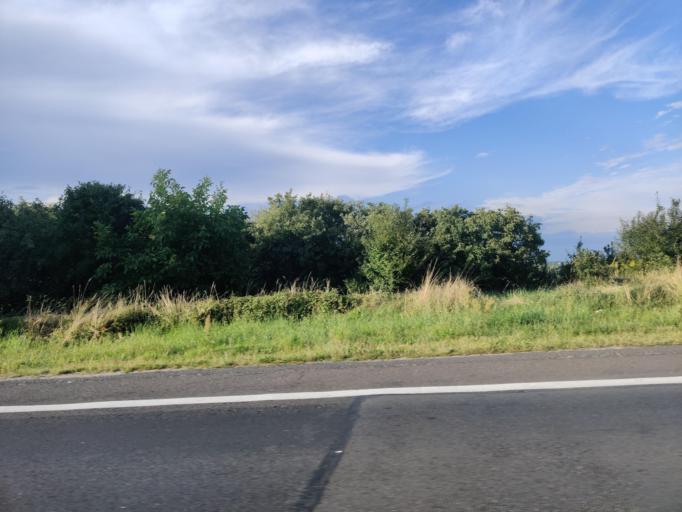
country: PL
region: Greater Poland Voivodeship
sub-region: Konin
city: Konin
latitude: 52.2002
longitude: 18.2862
